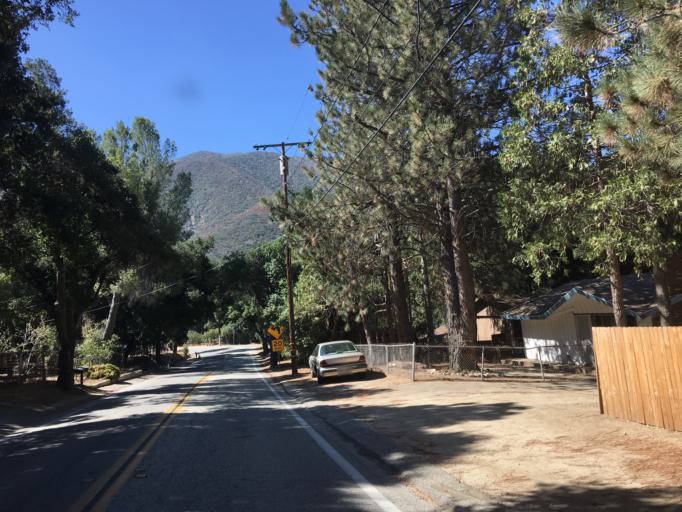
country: US
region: California
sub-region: Los Angeles County
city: Green Valley
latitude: 34.6207
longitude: -118.4139
